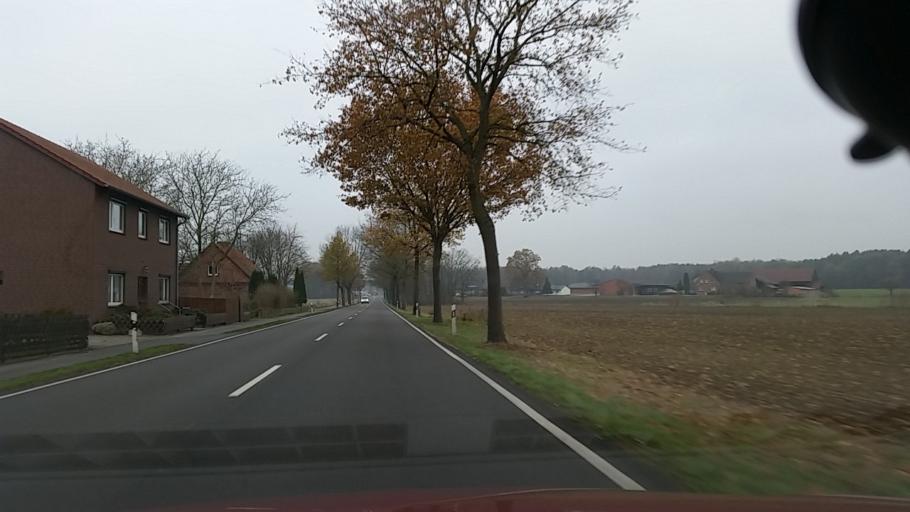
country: DE
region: Lower Saxony
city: Wittingen
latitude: 52.7283
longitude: 10.6807
